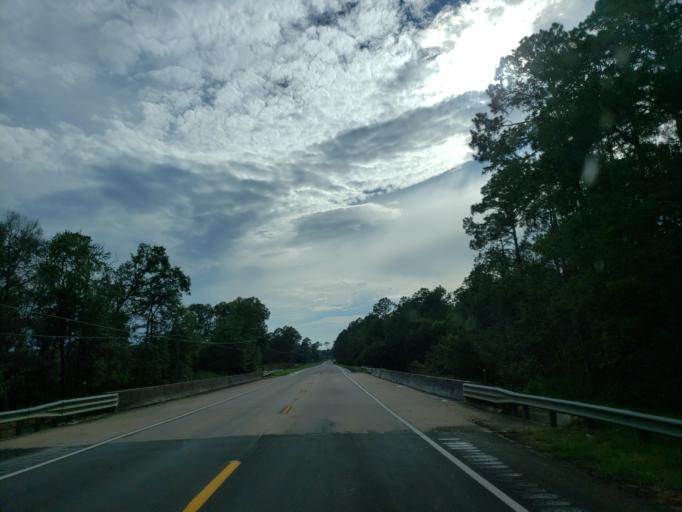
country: US
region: Georgia
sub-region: Irwin County
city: Ocilla
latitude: 31.5649
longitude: -83.3188
